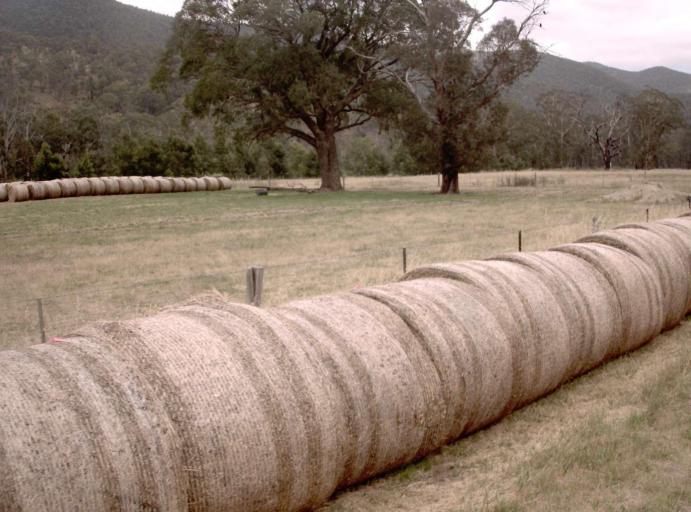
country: AU
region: Victoria
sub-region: Wellington
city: Heyfield
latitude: -37.6991
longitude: 146.6505
